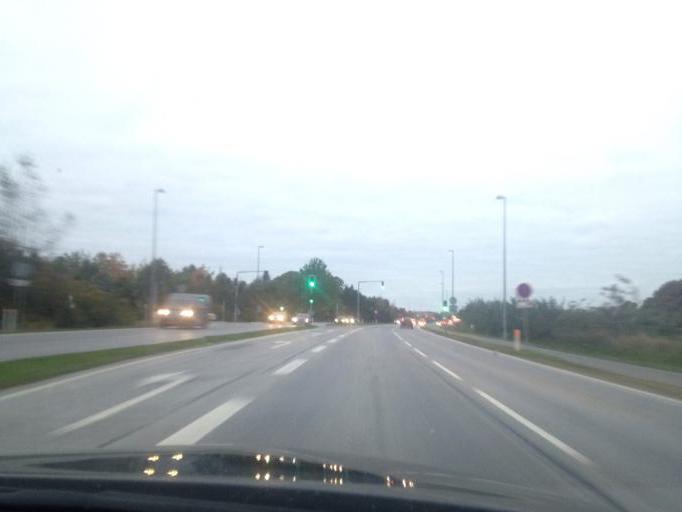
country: DK
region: Zealand
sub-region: Roskilde Kommune
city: Roskilde
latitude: 55.6192
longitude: 12.0937
